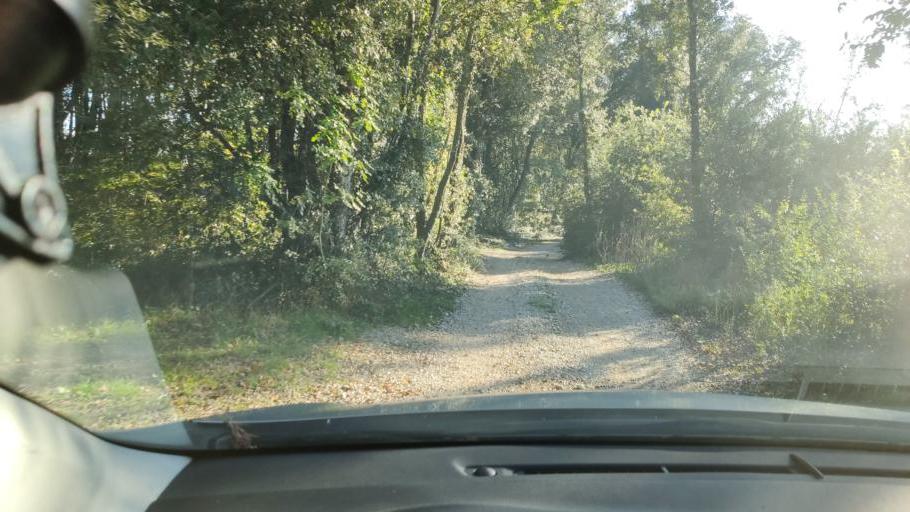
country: IT
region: Umbria
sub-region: Provincia di Terni
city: Amelia
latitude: 42.5789
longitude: 12.4358
